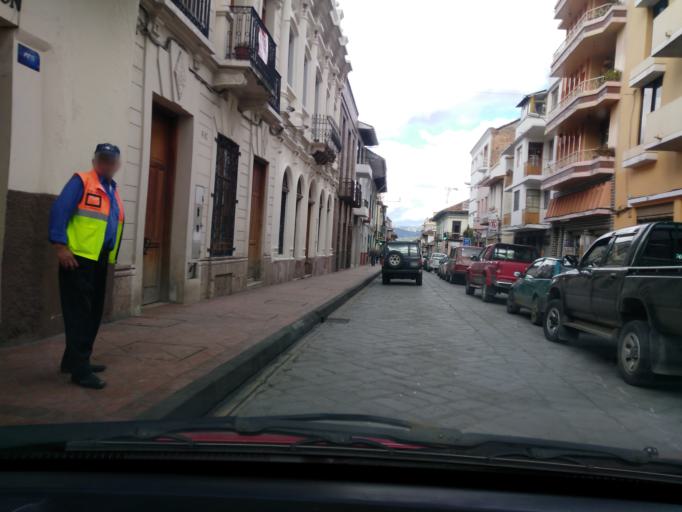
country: EC
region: Azuay
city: Cuenca
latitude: -2.8996
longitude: -79.0060
